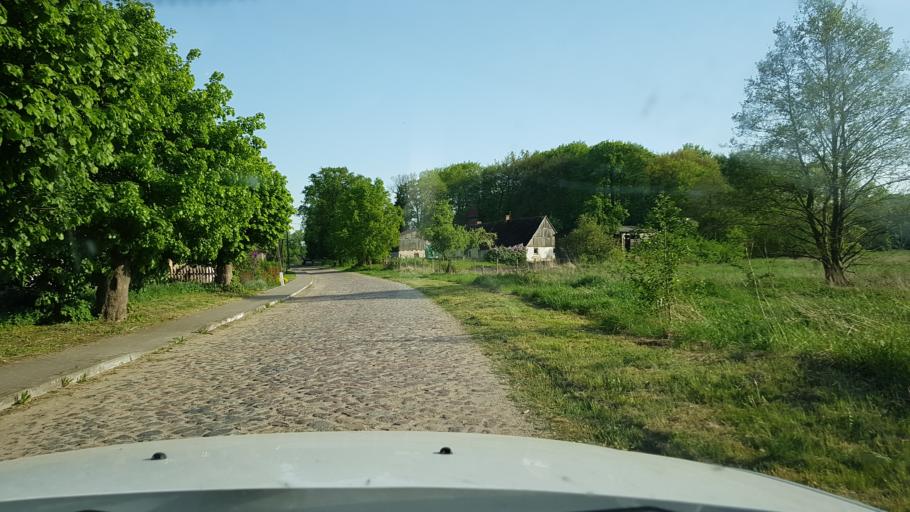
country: PL
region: West Pomeranian Voivodeship
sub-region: Powiat lobeski
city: Resko
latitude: 53.7088
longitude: 15.3338
